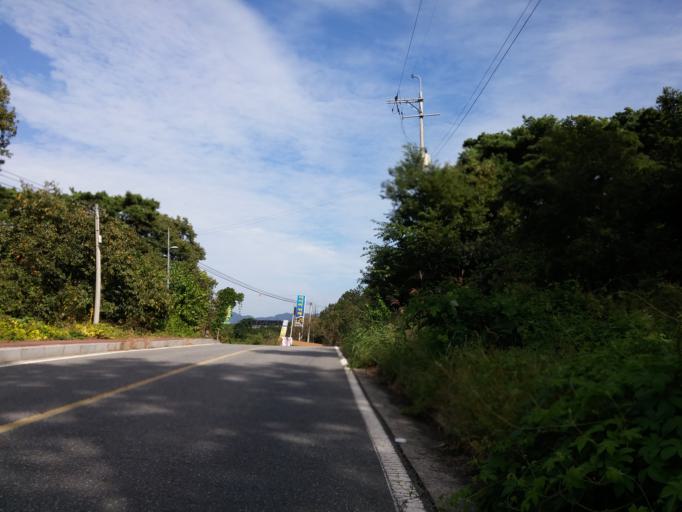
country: KR
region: Chungcheongnam-do
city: Yonmu
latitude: 36.1726
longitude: 127.1650
